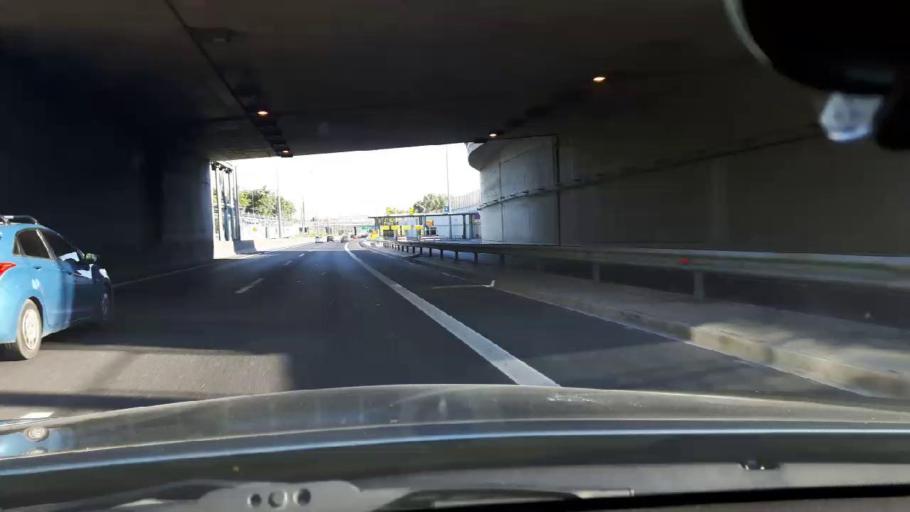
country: GR
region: Attica
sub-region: Nomarchia Anatolikis Attikis
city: Pallini
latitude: 37.9943
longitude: 23.8725
